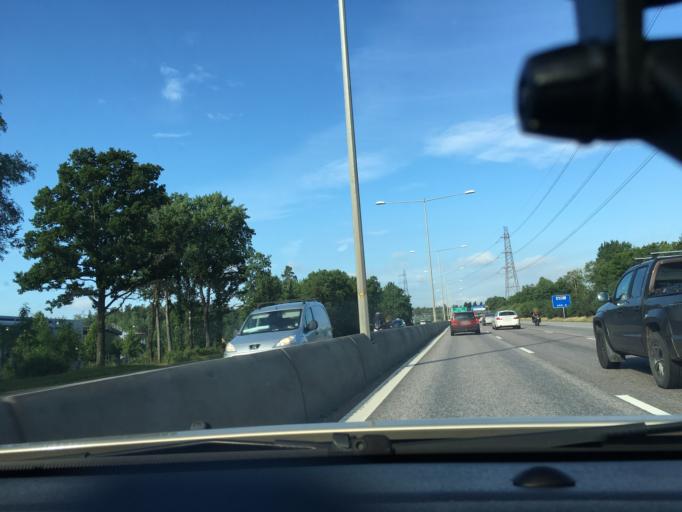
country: SE
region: Stockholm
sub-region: Huddinge Kommun
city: Segeltorp
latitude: 59.2839
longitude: 17.9311
